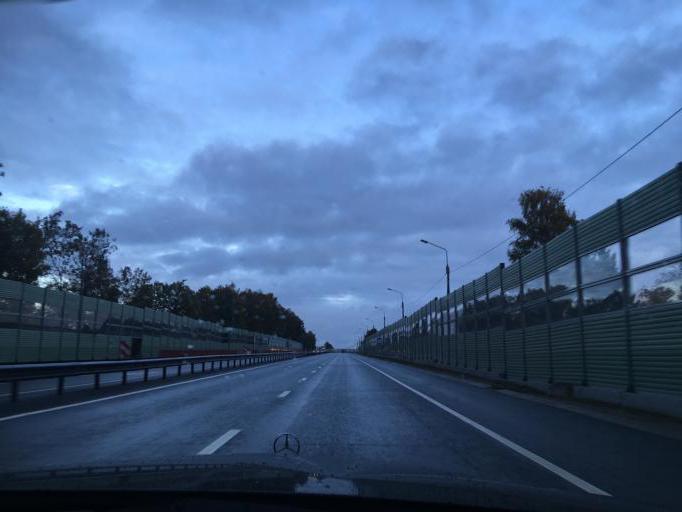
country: RU
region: Smolensk
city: Yartsevo
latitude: 55.0791
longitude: 32.6986
